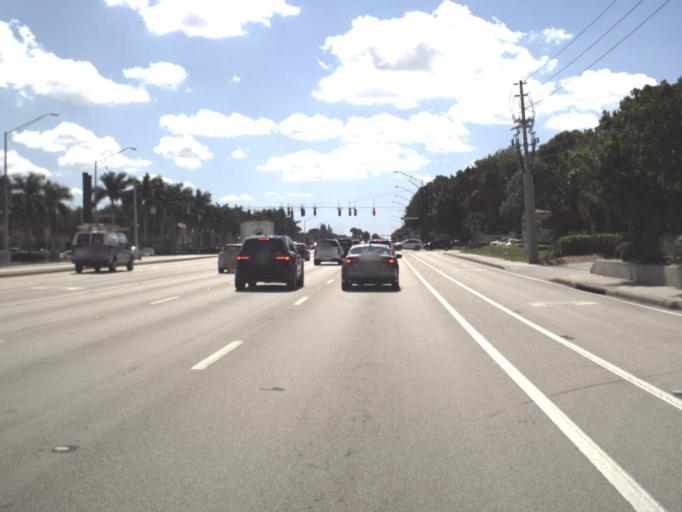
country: US
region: Florida
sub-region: Collier County
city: Naples Park
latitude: 26.2520
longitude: -81.8013
